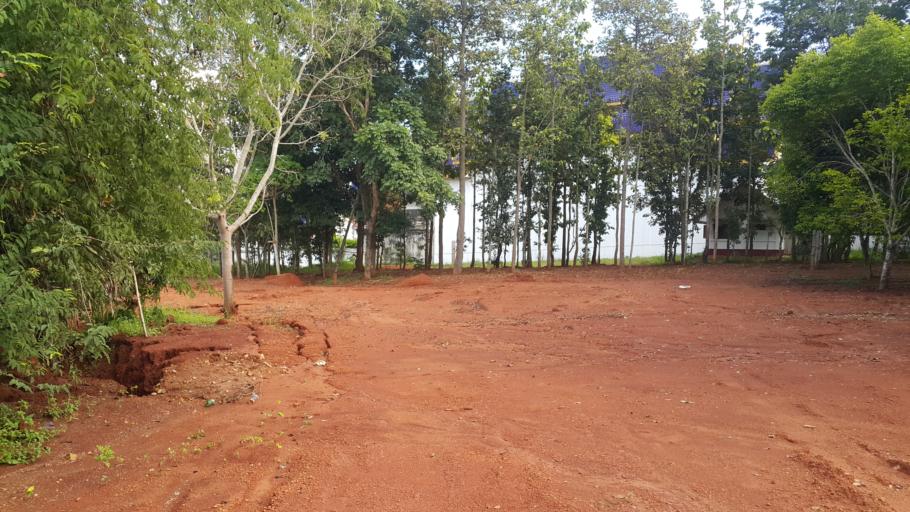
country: TH
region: Chiang Mai
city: Mae Taeng
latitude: 19.1590
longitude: 98.9776
